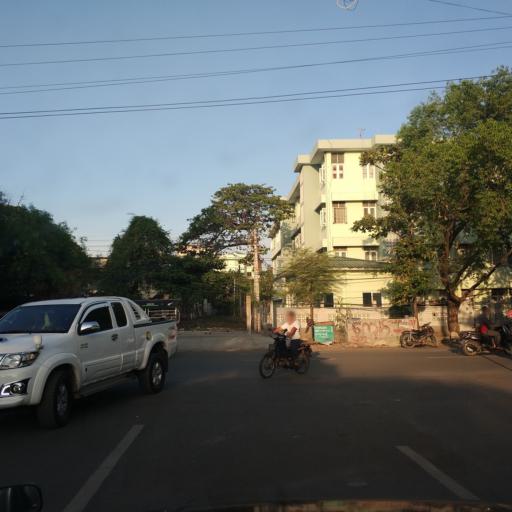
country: MM
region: Mandalay
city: Mandalay
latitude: 21.9749
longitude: 96.0932
